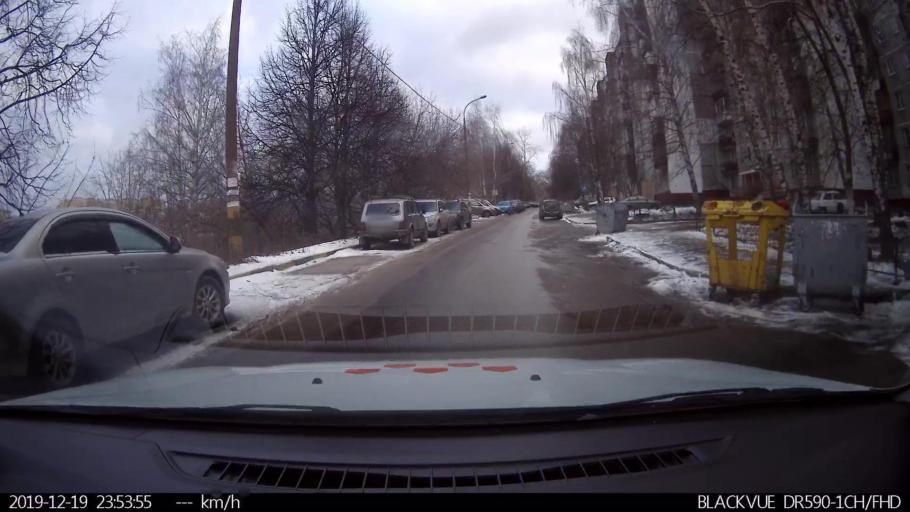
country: RU
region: Vologda
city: Molochnoye
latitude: 58.9481
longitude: 39.5067
